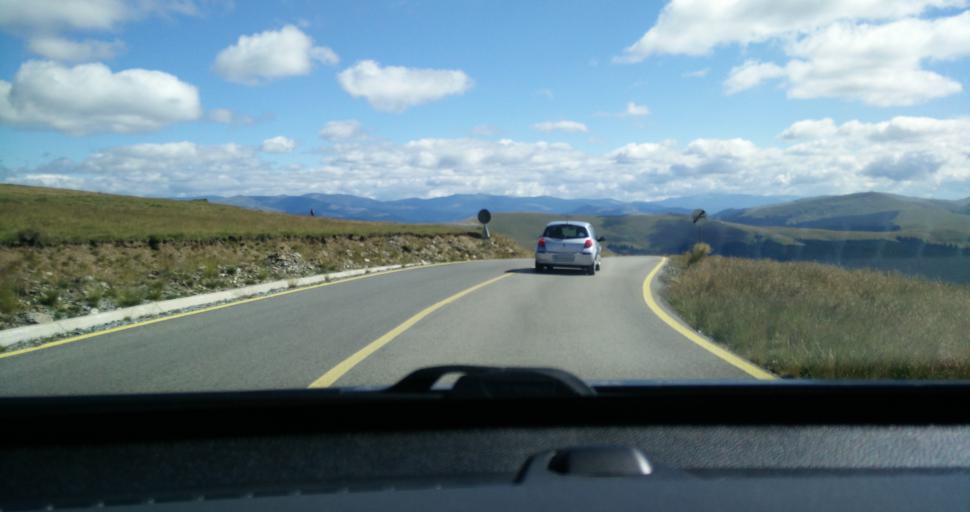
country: RO
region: Gorj
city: Novaci-Straini
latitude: 45.3691
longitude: 23.6507
